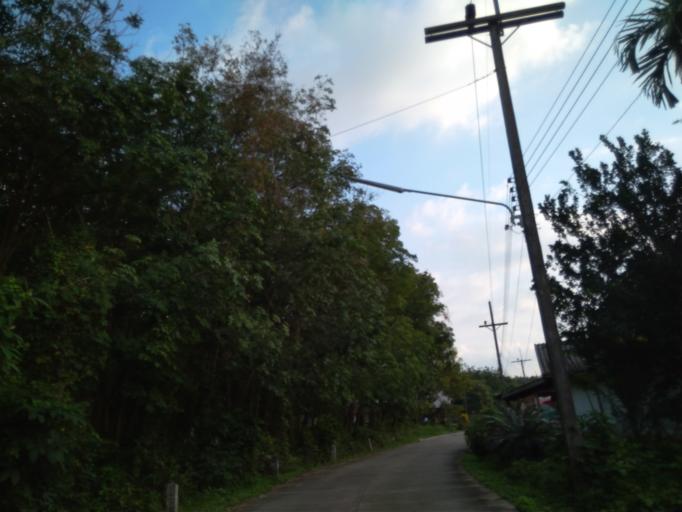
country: TH
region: Phangnga
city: Ko Yao
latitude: 8.1436
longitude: 98.5987
